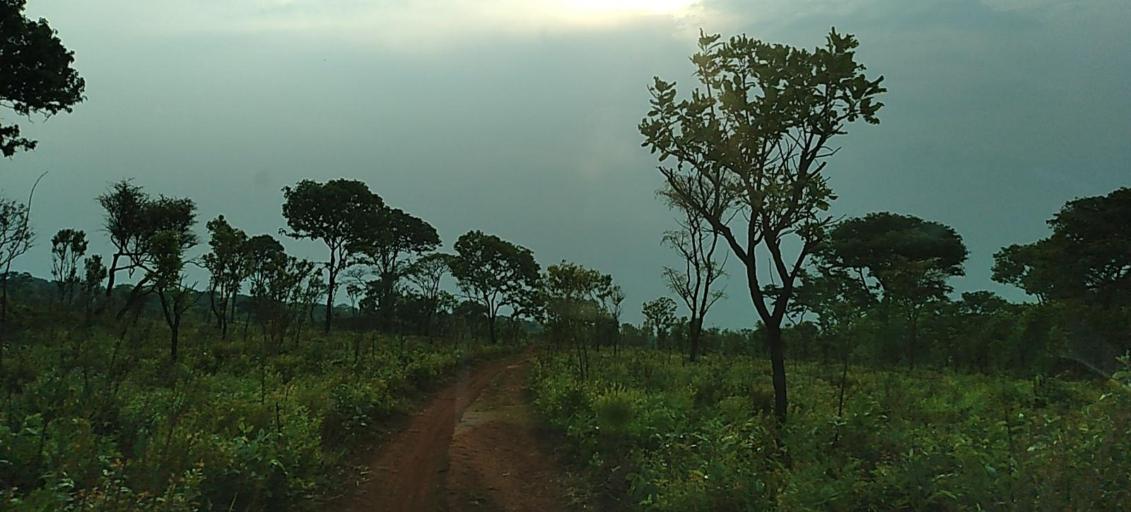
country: ZM
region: North-Western
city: Solwezi
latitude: -12.0426
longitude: 26.0308
